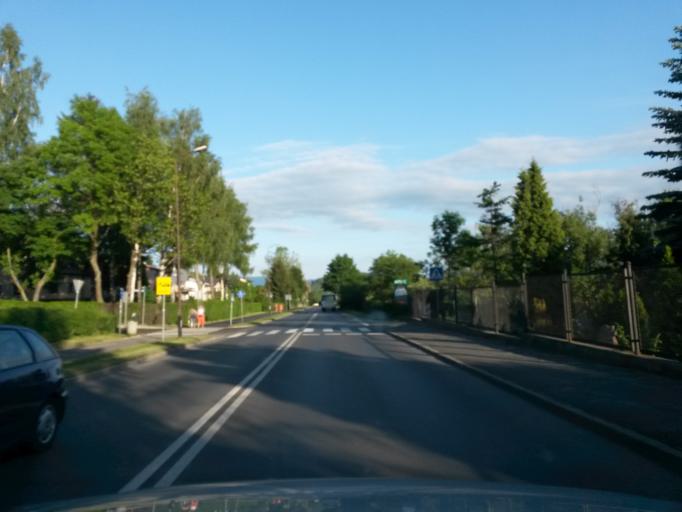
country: PL
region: Lower Silesian Voivodeship
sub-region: Jelenia Gora
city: Jelenia Gora
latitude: 50.8921
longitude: 15.7481
